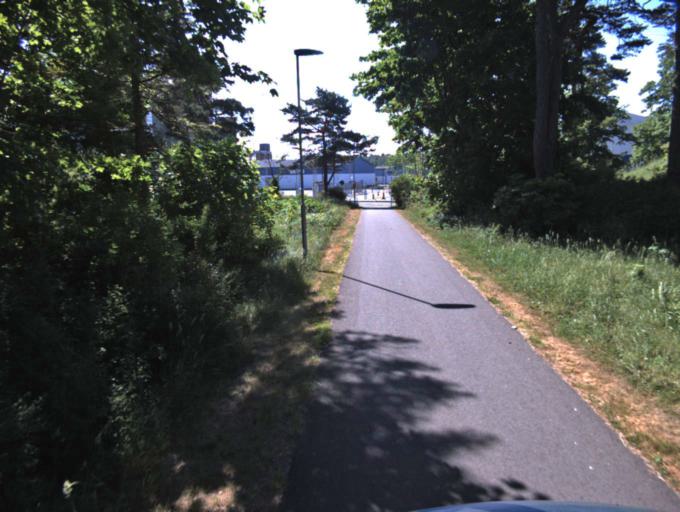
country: SE
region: Skane
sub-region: Kristianstads Kommun
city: Ahus
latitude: 55.9294
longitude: 14.3134
